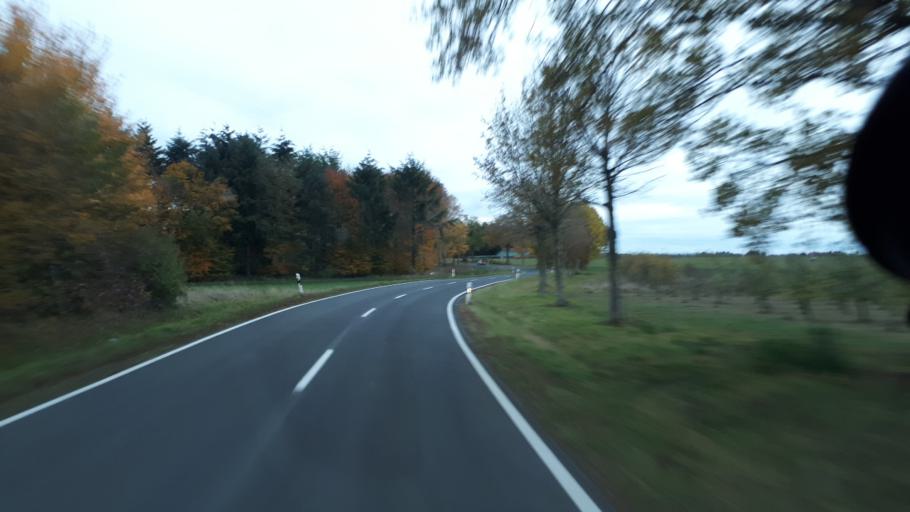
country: DE
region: Rheinland-Pfalz
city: Alflen
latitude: 50.1840
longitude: 7.0366
